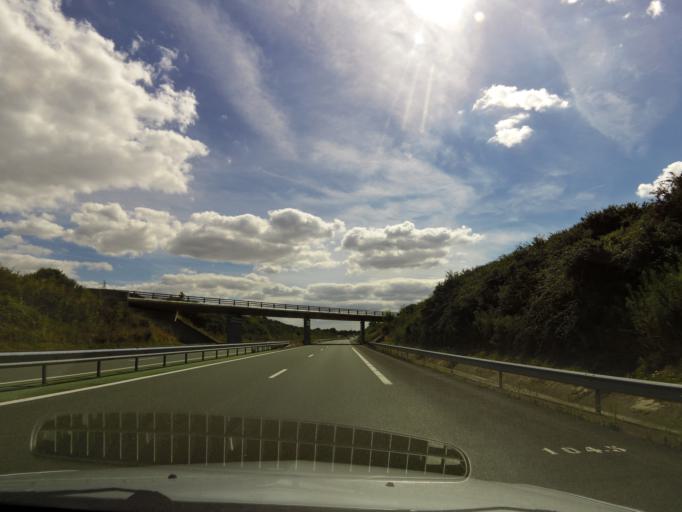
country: FR
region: Pays de la Loire
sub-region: Departement de la Vendee
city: La Ferriere
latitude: 46.7213
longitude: -1.2792
